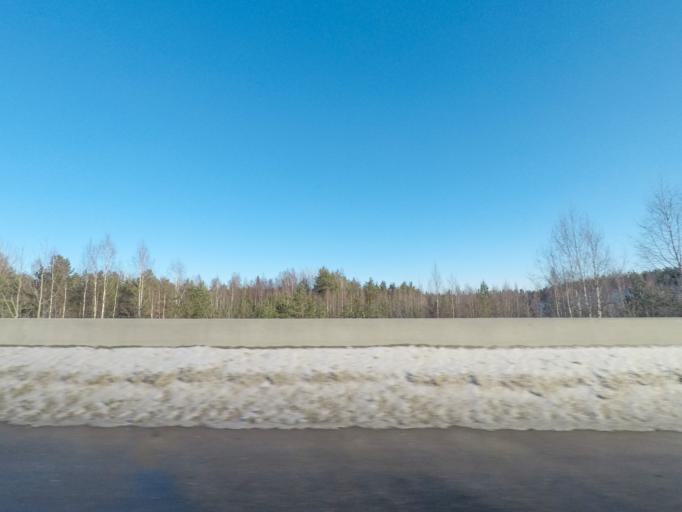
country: FI
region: Paijanne Tavastia
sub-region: Lahti
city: Nastola
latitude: 61.0074
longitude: 25.8114
